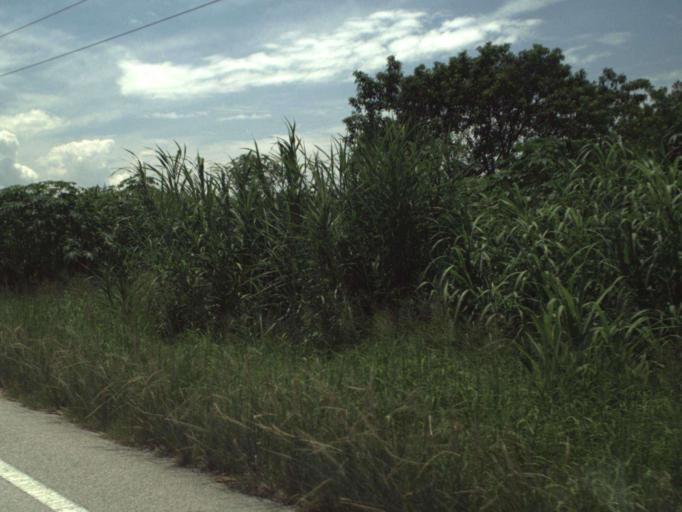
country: US
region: Florida
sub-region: Palm Beach County
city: Pahokee
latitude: 26.8960
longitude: -80.6120
